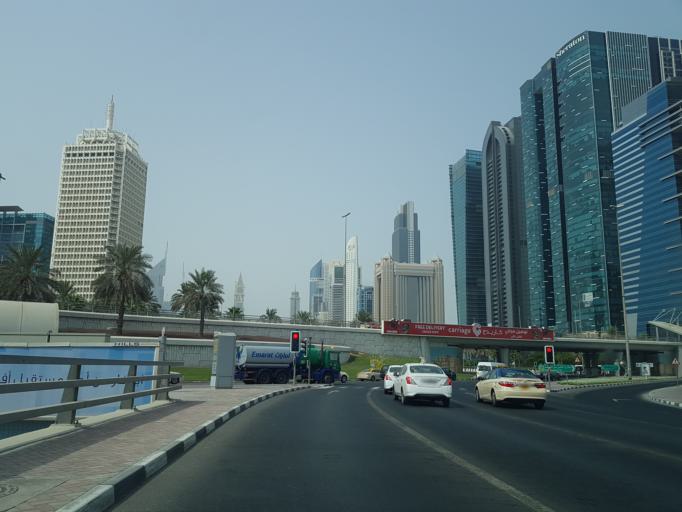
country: AE
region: Ash Shariqah
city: Sharjah
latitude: 25.2307
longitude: 55.2899
